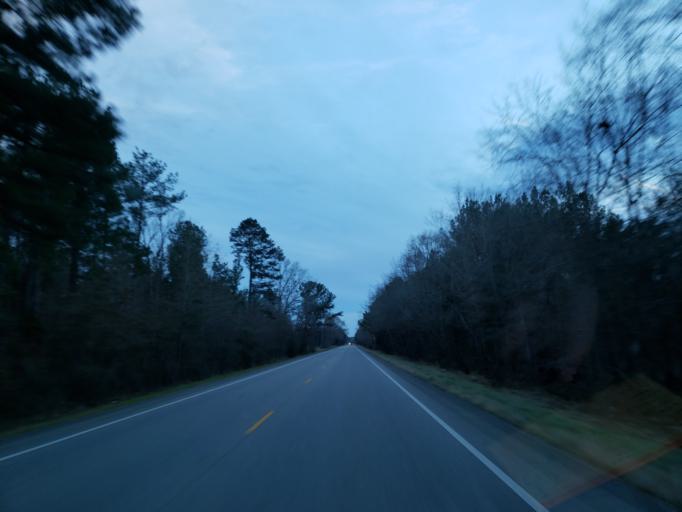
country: US
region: Alabama
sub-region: Sumter County
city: Livingston
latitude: 32.8218
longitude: -88.3104
